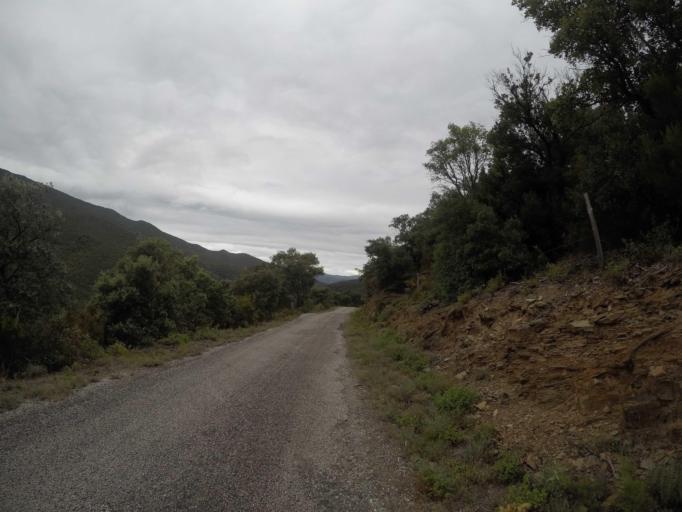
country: FR
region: Languedoc-Roussillon
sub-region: Departement des Pyrenees-Orientales
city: Ille-sur-Tet
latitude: 42.6129
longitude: 2.6076
